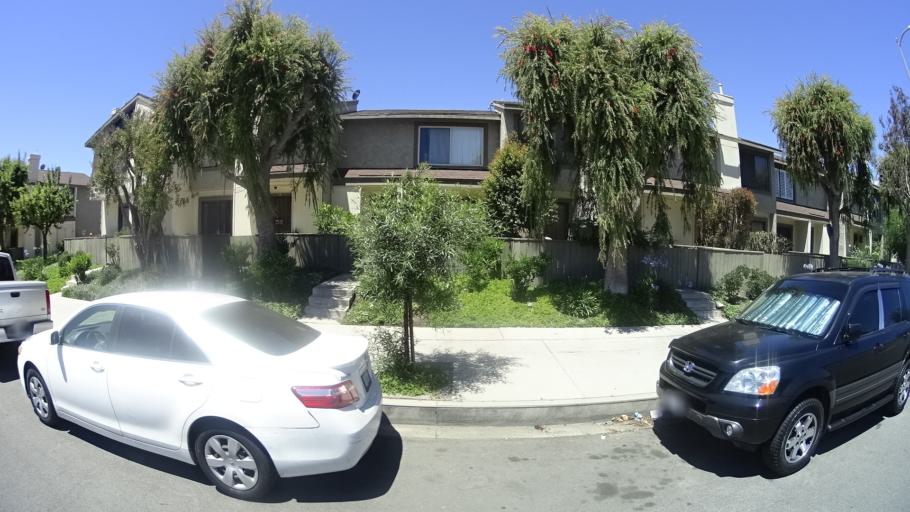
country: US
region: California
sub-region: Los Angeles County
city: San Fernando
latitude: 34.2449
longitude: -118.4677
